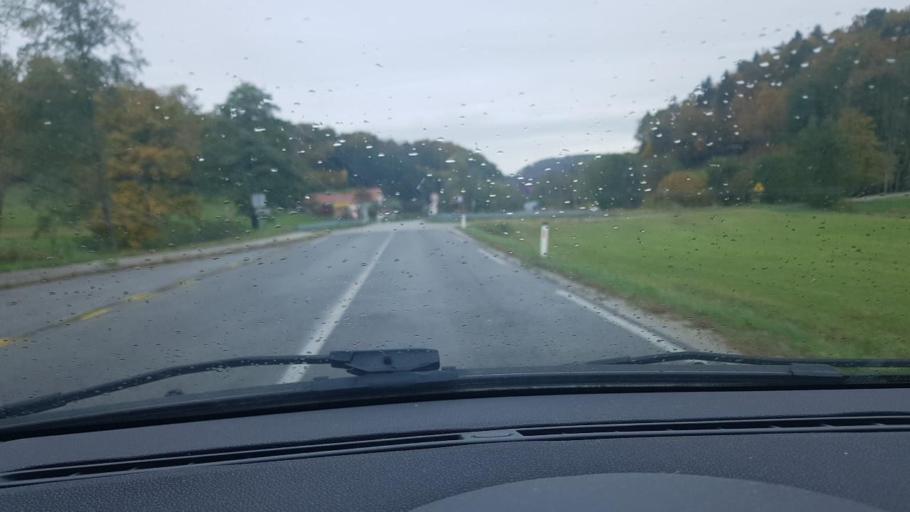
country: SI
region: Rogatec
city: Rogatec
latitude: 46.2524
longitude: 15.7011
